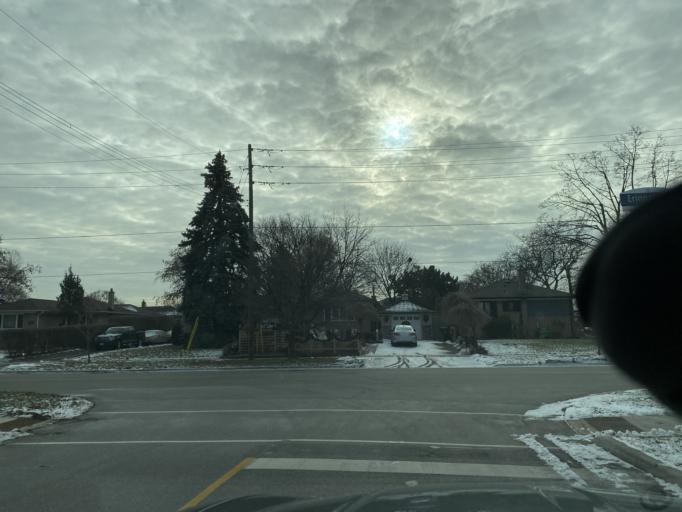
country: CA
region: Ontario
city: Etobicoke
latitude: 43.6627
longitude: -79.5757
